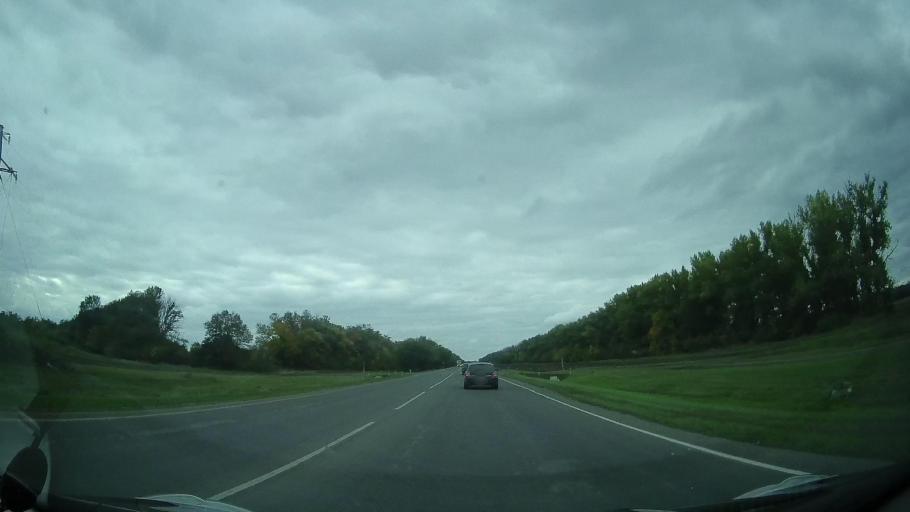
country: RU
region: Rostov
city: Yegorlykskaya
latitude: 46.6003
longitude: 40.6186
